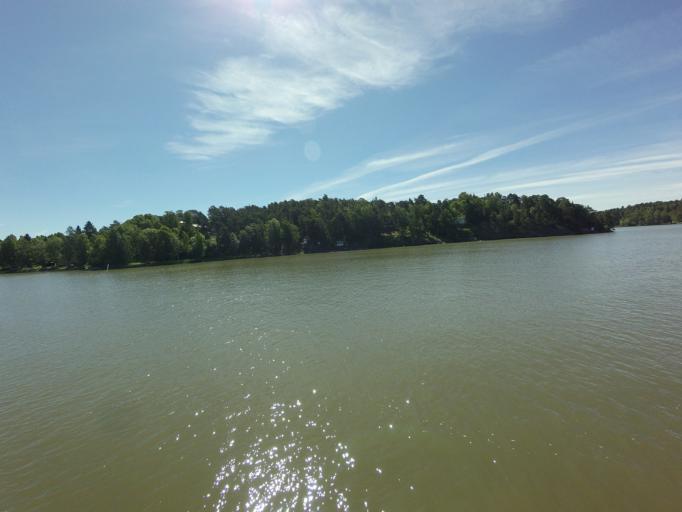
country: FI
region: Varsinais-Suomi
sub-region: Turku
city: Raisio
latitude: 60.4231
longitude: 22.1776
